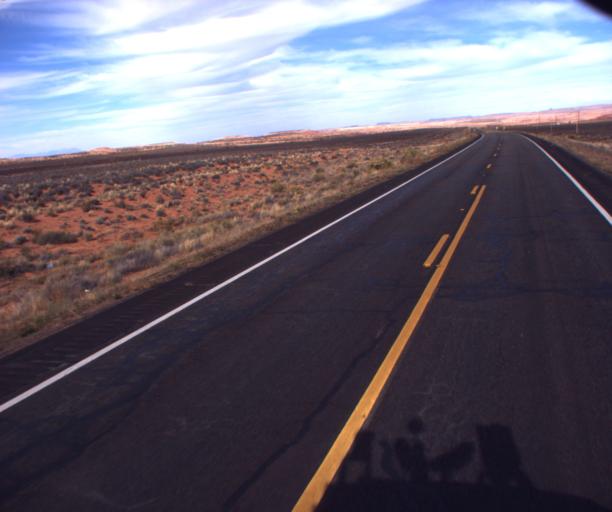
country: US
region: Arizona
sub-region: Navajo County
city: Kayenta
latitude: 36.9186
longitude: -109.7675
